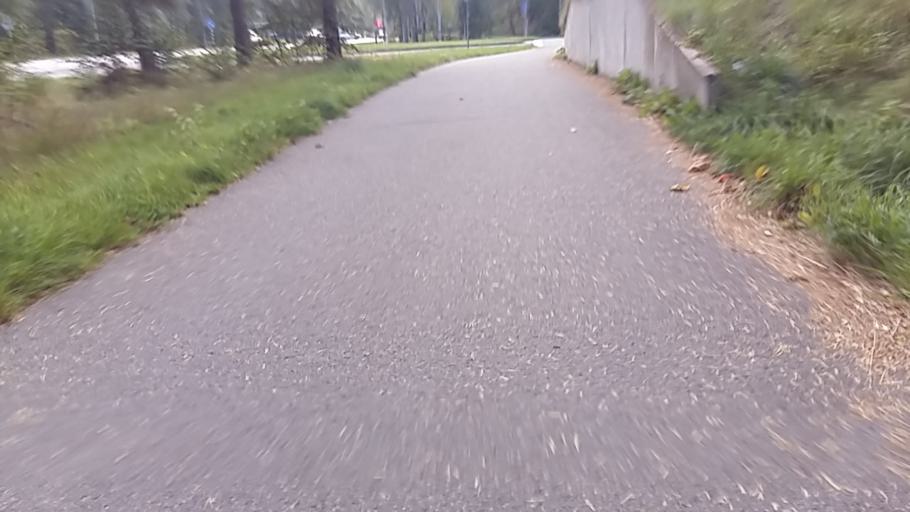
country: SE
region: Joenkoeping
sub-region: Jonkopings Kommun
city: Odensjo
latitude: 57.7431
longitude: 14.1568
